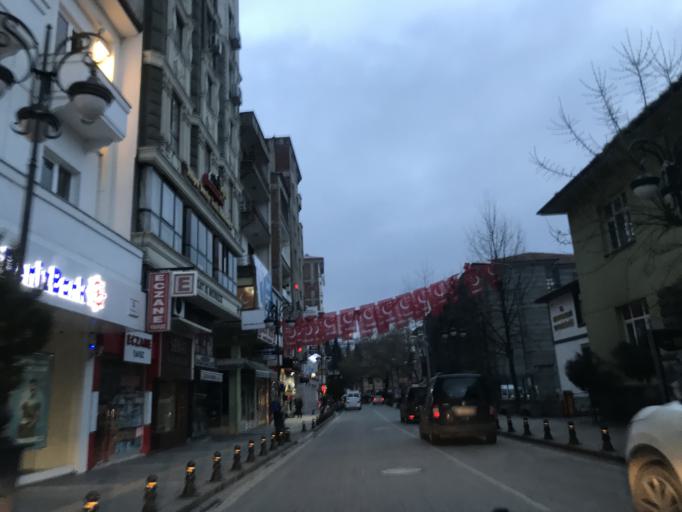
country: TR
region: Trabzon
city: Akcaabat
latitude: 41.0226
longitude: 39.5681
